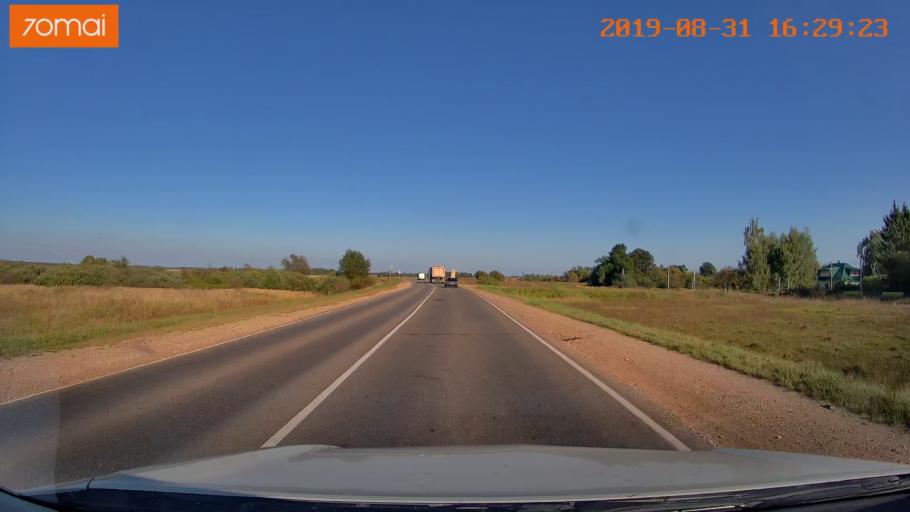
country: RU
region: Kaluga
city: Babynino
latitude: 54.5059
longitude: 35.8038
